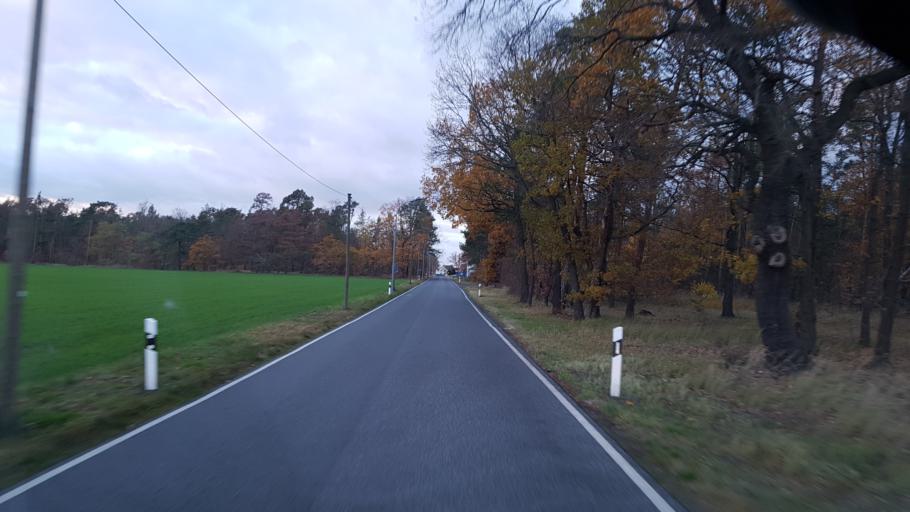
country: DE
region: Brandenburg
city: Tettau
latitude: 51.4255
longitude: 13.7405
